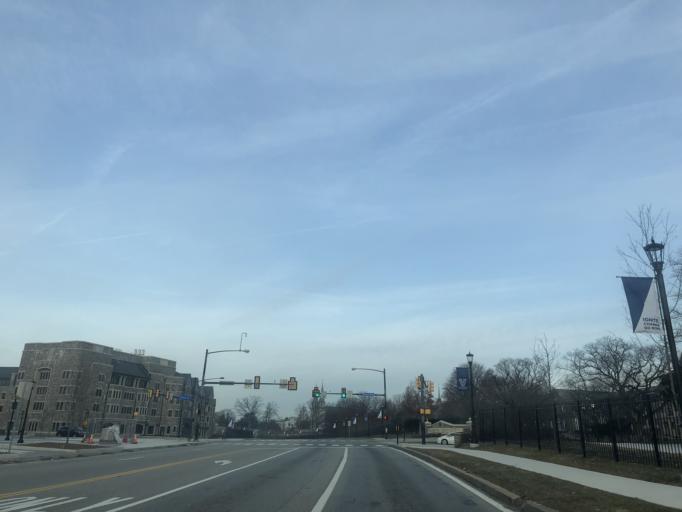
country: US
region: Pennsylvania
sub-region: Delaware County
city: Radnor
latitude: 40.0334
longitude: -75.3386
